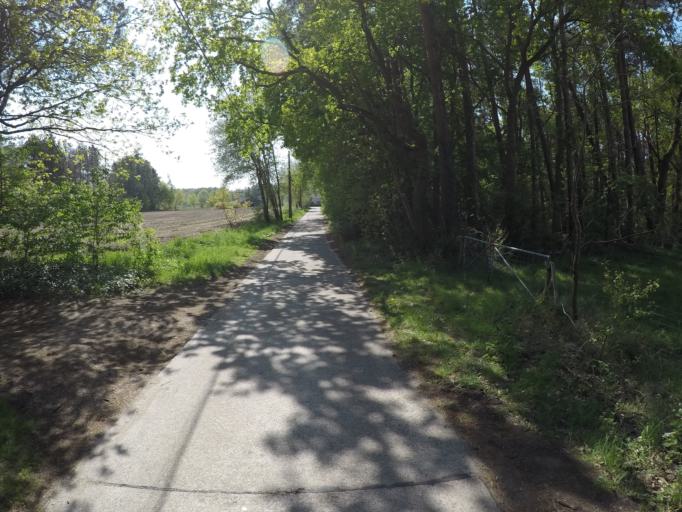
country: BE
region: Flanders
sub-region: Provincie Antwerpen
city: Zandhoven
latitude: 51.2499
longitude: 4.6615
